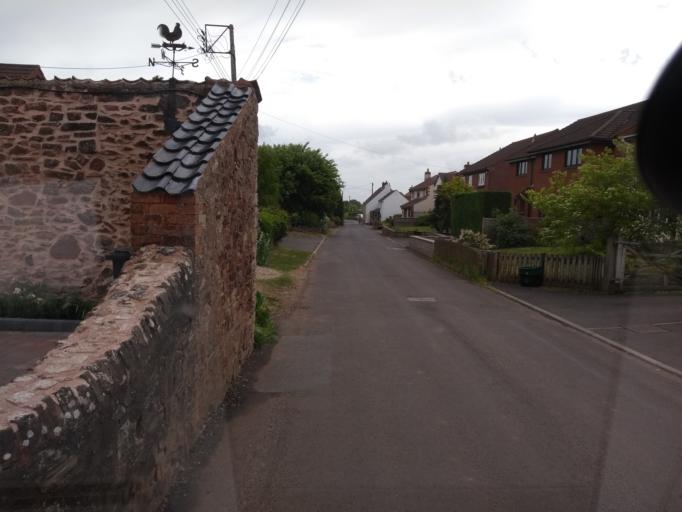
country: GB
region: England
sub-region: Somerset
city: Bishops Lydeard
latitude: 51.1234
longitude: -3.1119
